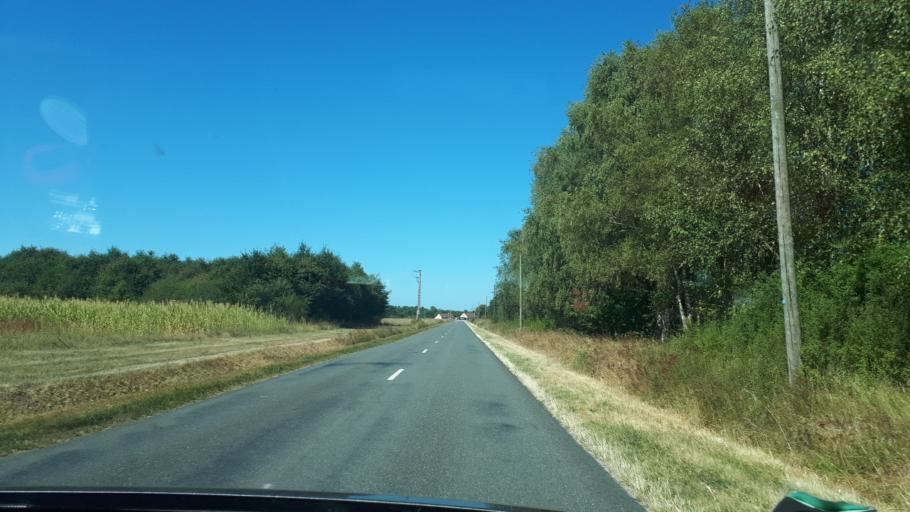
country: FR
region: Centre
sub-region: Departement du Loiret
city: Coullons
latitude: 47.6369
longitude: 2.4295
